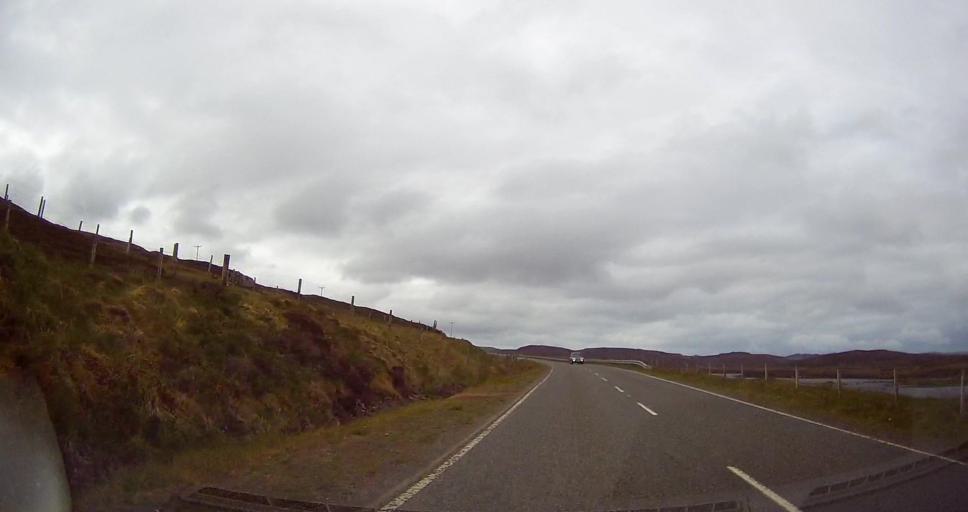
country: GB
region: Scotland
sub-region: Shetland Islands
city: Lerwick
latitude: 60.2558
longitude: -1.4657
